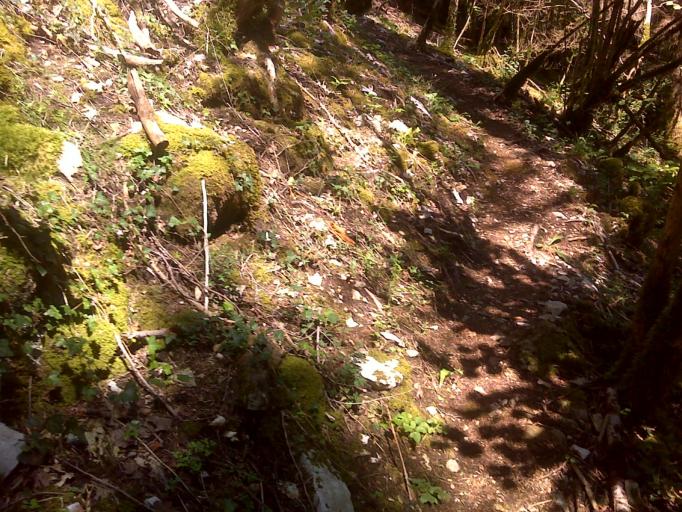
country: FR
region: Rhone-Alpes
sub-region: Departement de l'Ain
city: Montreal-la-Cluse
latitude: 46.1696
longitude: 5.6003
